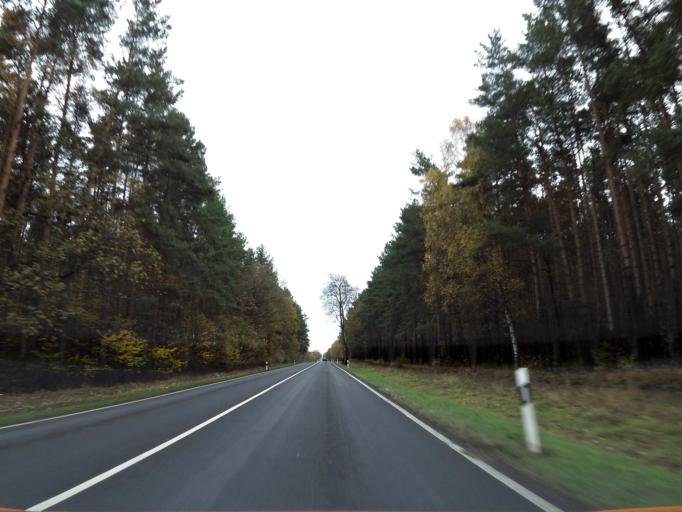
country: DE
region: Saxony-Anhalt
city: Letzlingen
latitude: 52.3888
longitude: 11.4691
